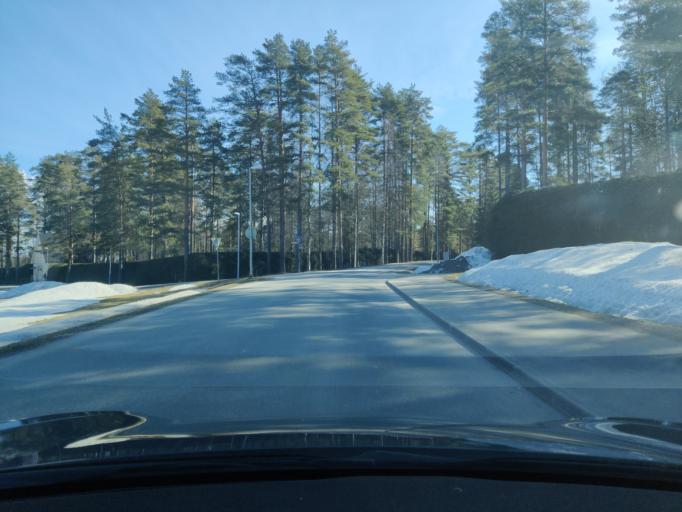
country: FI
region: Northern Savo
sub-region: Kuopio
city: Vehmersalmi
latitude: 62.7605
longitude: 28.0333
